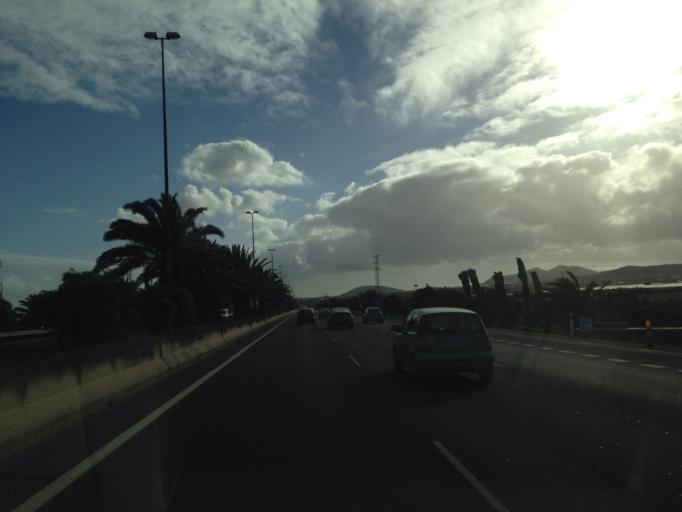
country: ES
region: Canary Islands
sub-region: Provincia de Las Palmas
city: Ingenio
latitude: 27.9378
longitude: -15.3920
